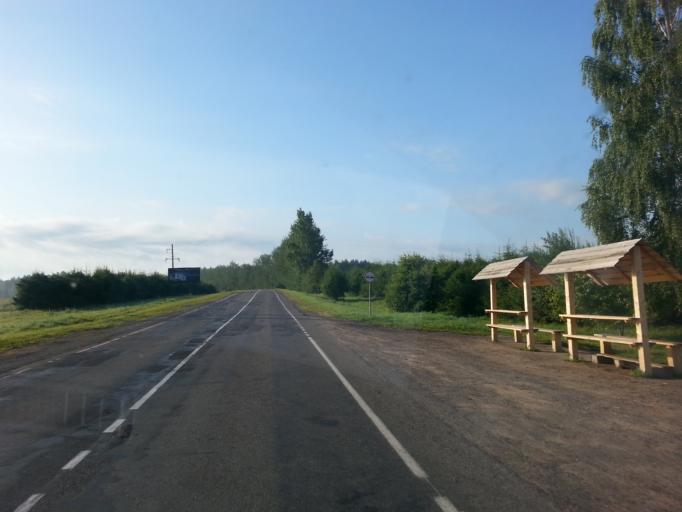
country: BY
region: Minsk
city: Kryvichy
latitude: 54.7550
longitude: 27.1068
